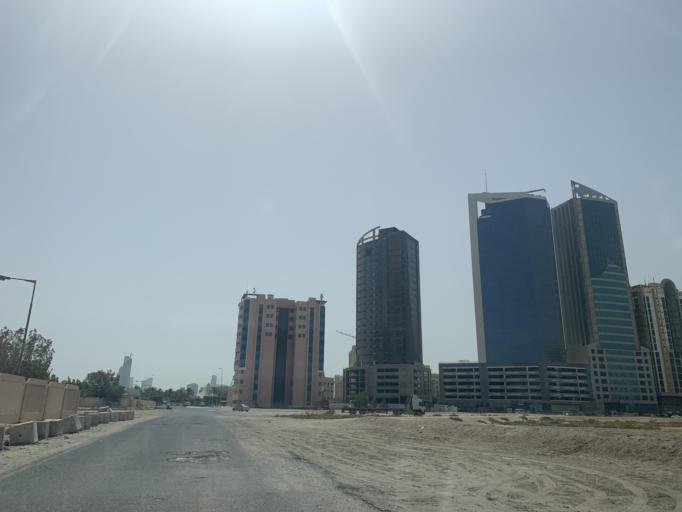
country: BH
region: Manama
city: Jidd Hafs
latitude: 26.2425
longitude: 50.5339
